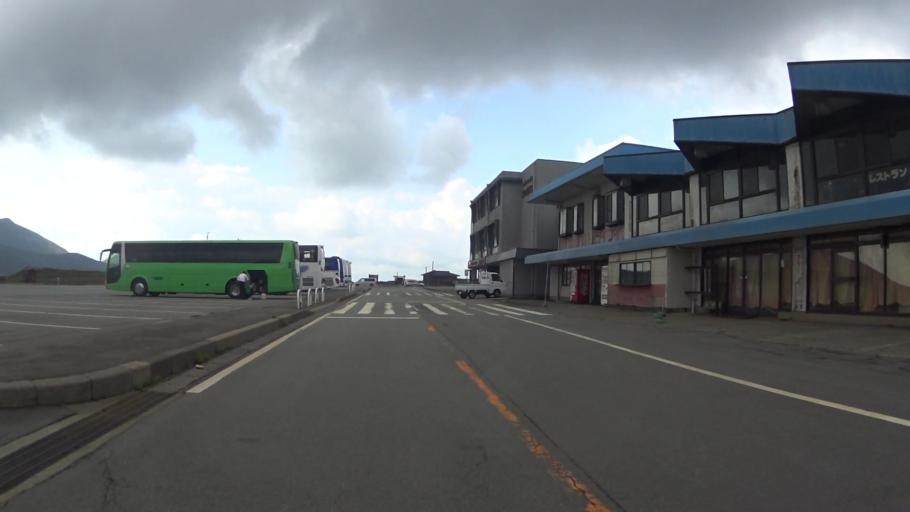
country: JP
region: Kumamoto
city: Aso
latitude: 32.8792
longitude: 131.0738
